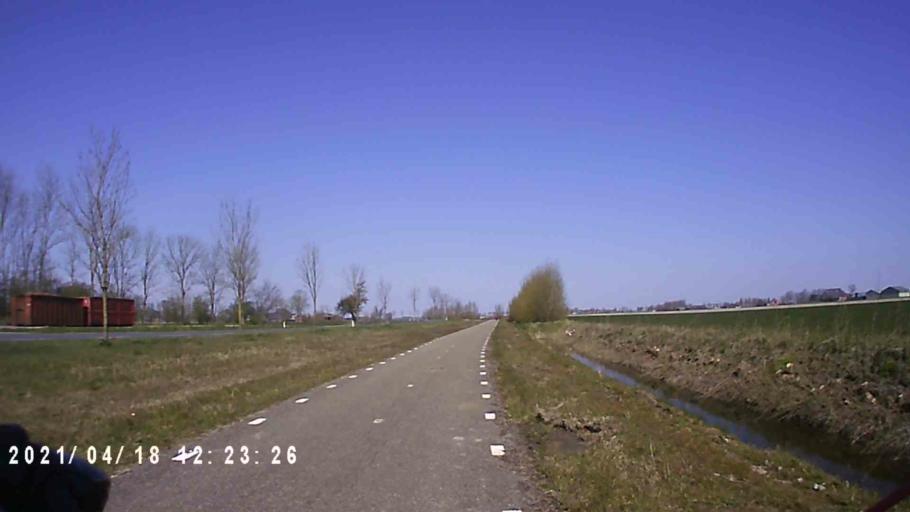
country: NL
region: Friesland
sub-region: Gemeente Dongeradeel
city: Anjum
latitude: 53.3252
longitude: 6.1221
